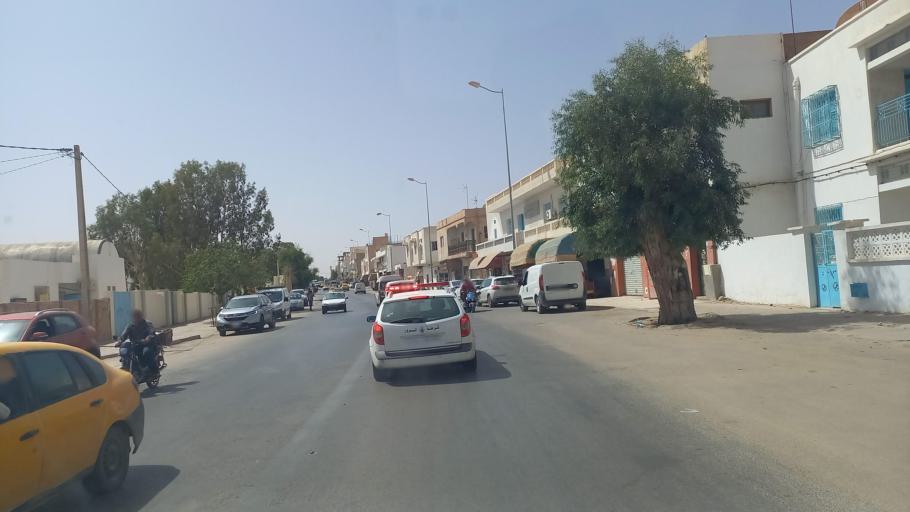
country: TN
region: Madanin
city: Medenine
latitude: 33.3365
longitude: 10.4857
